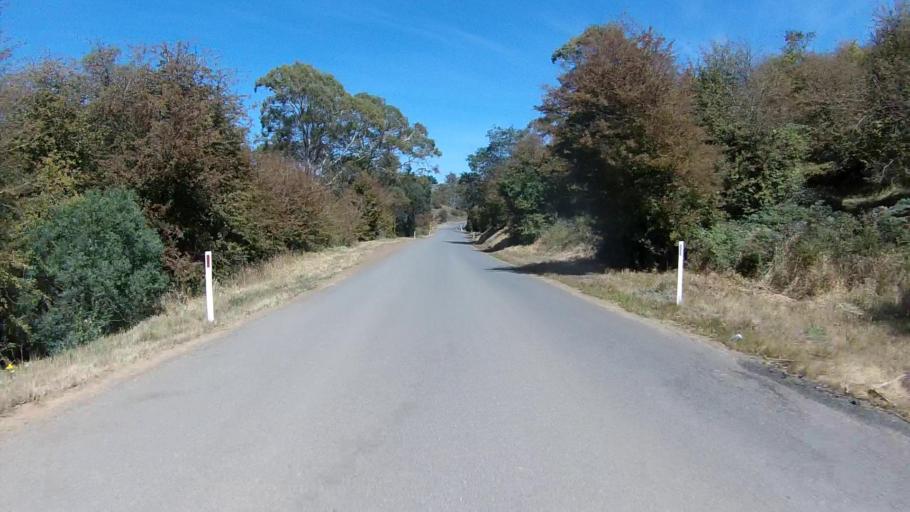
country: AU
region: Tasmania
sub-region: Sorell
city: Sorell
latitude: -42.7585
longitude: 147.6567
